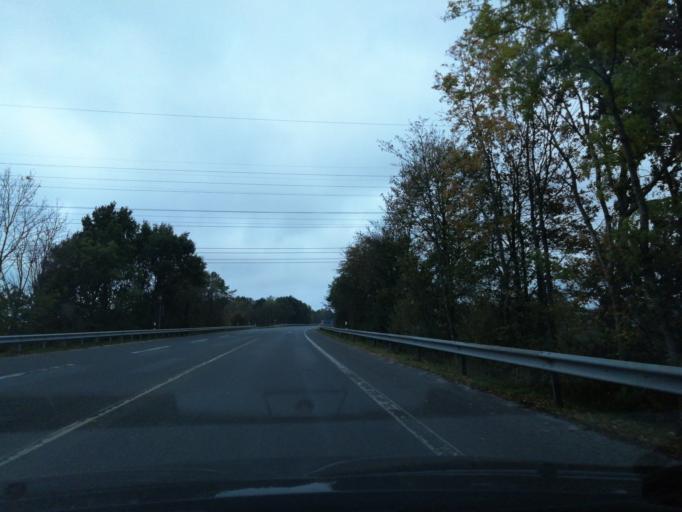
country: DE
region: Lower Saxony
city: Fedderwarden
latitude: 53.5436
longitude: 8.0509
